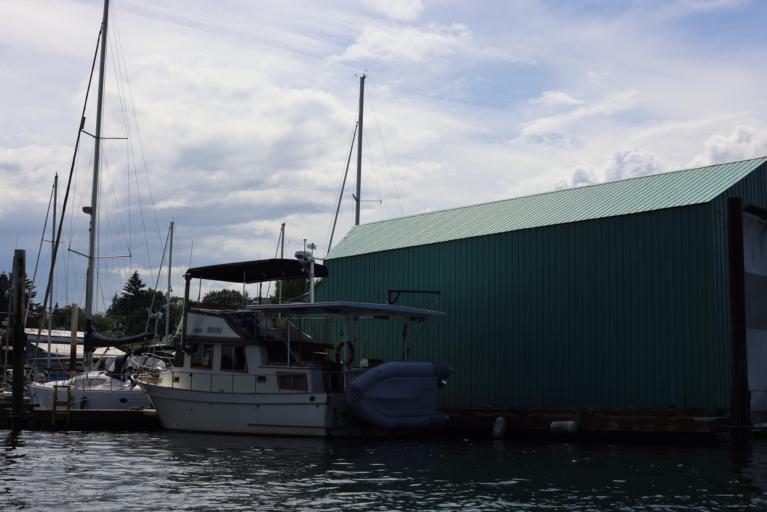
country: CA
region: British Columbia
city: Nanaimo
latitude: 49.1837
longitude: -123.9437
